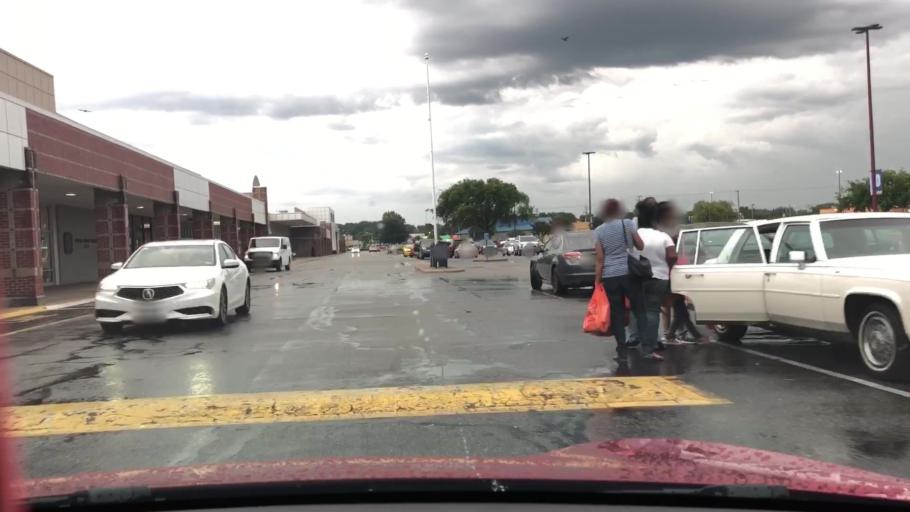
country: US
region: Virginia
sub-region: City of Chesapeake
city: Chesapeake
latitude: 36.8584
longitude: -76.2041
